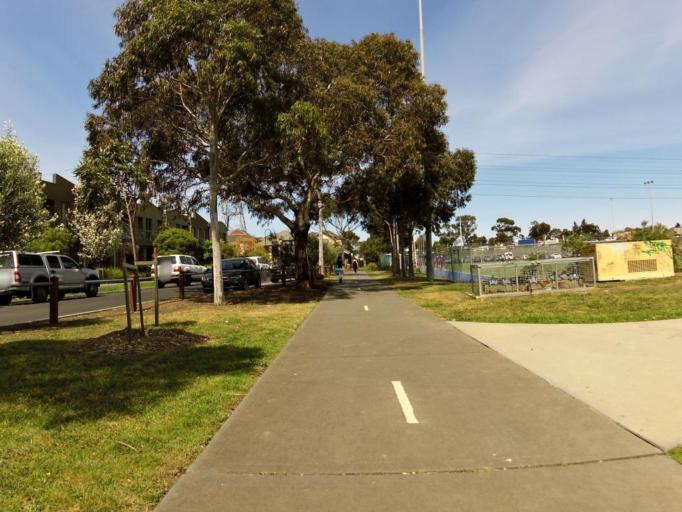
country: AU
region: Victoria
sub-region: Hobsons Bay
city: South Kingsville
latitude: -37.8225
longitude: 144.8714
